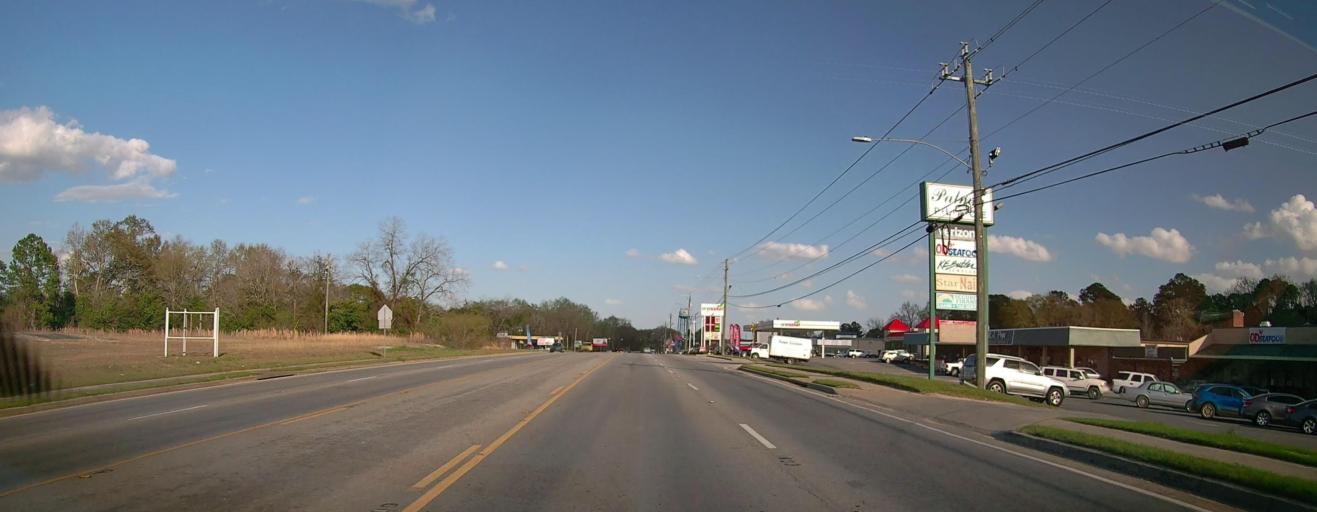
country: US
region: Georgia
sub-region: Toombs County
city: Vidalia
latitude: 32.2118
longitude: -82.3978
